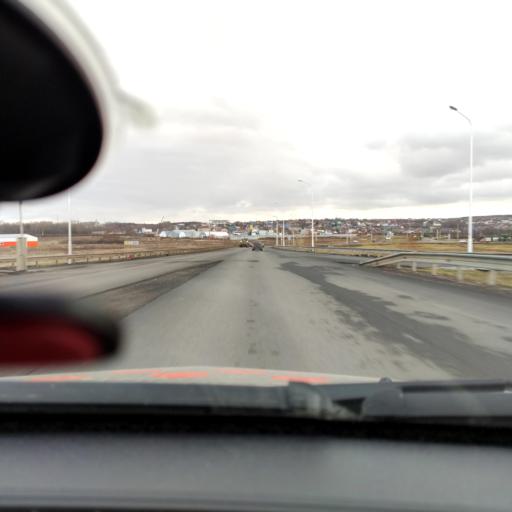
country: RU
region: Bashkortostan
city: Kabakovo
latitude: 54.6488
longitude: 56.0832
